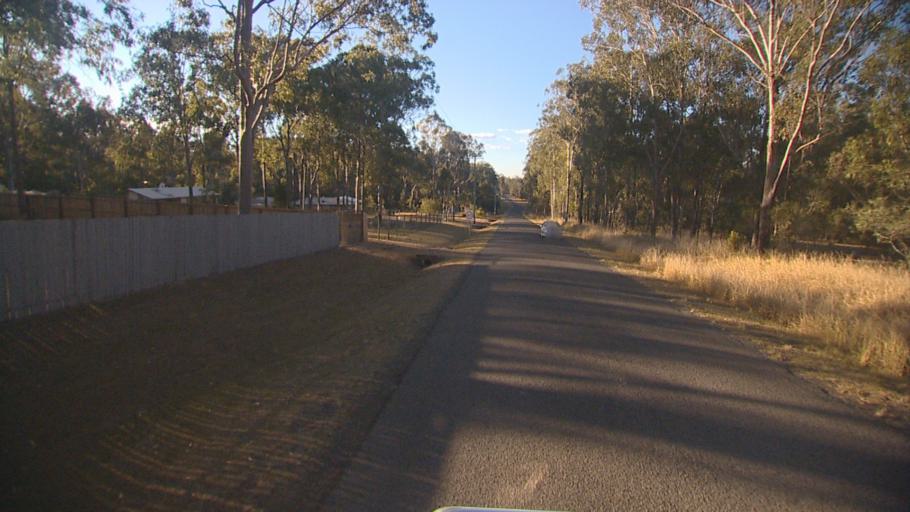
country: AU
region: Queensland
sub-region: Logan
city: Cedar Vale
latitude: -27.8688
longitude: 152.9758
